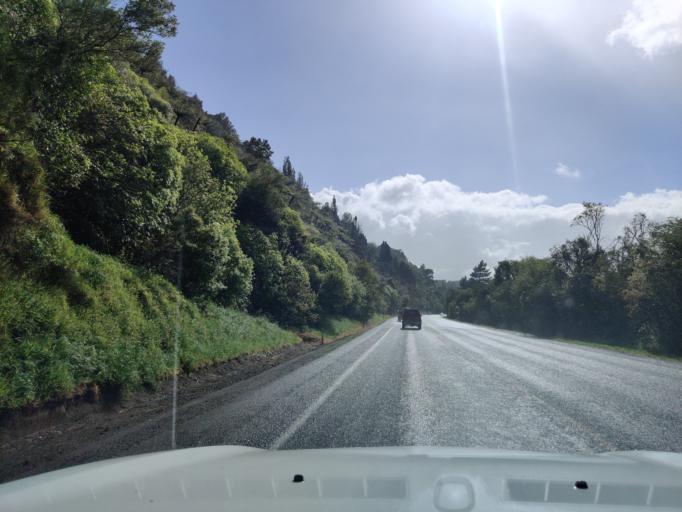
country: NZ
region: Waikato
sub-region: Matamata-Piako District
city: Matamata
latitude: -37.9486
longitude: 175.6392
